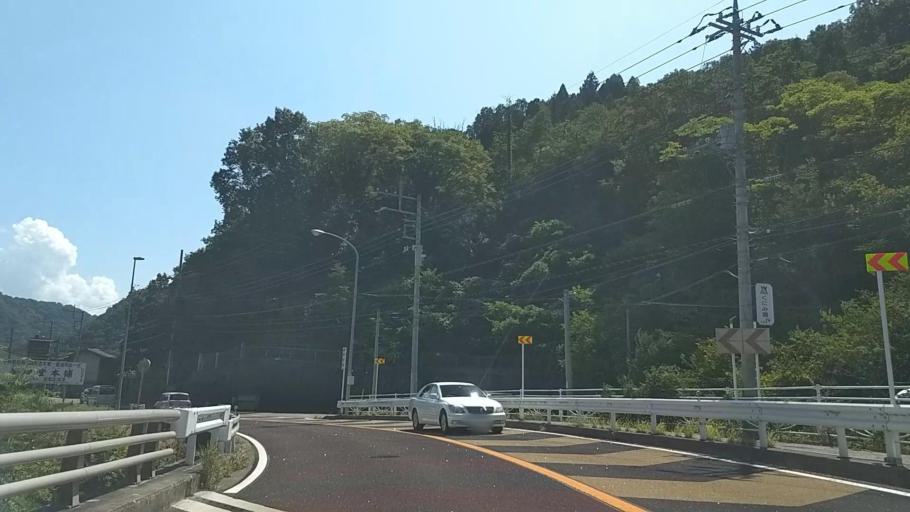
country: JP
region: Yamanashi
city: Ryuo
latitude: 35.5256
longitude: 138.4495
